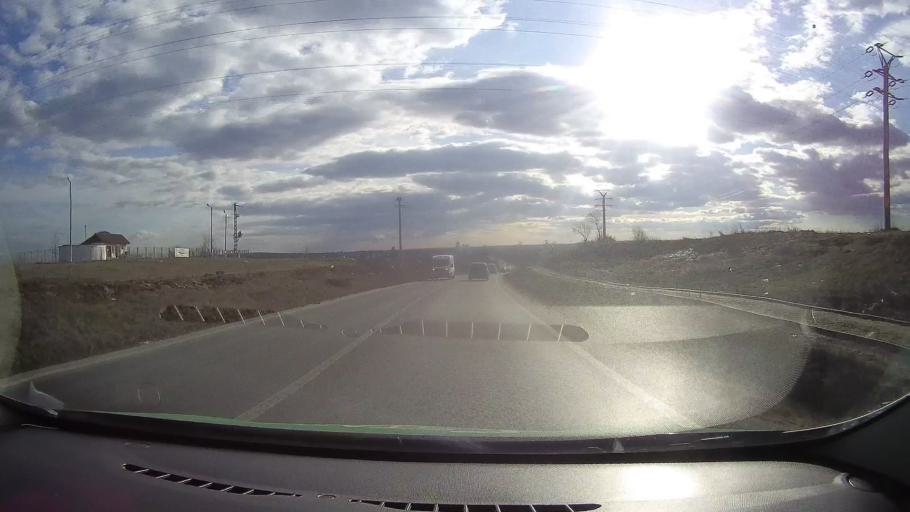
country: RO
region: Dambovita
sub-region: Comuna Lucieni
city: Lucieni
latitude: 44.8509
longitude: 25.4340
